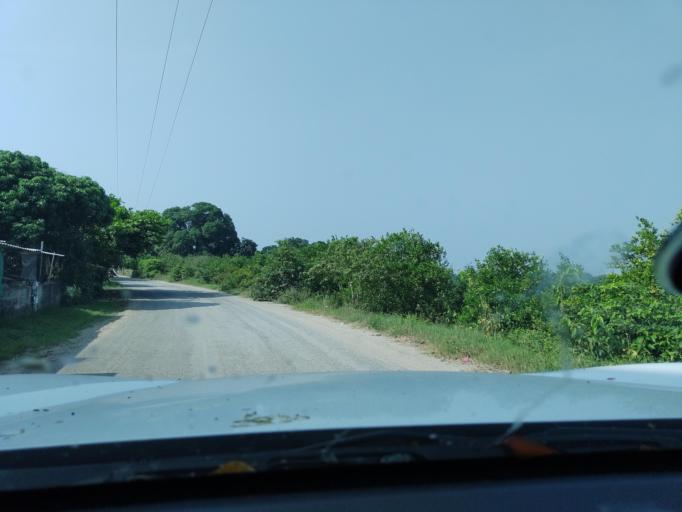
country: MX
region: Veracruz
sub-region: Martinez de la Torre
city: El Progreso
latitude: 20.0780
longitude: -97.0054
